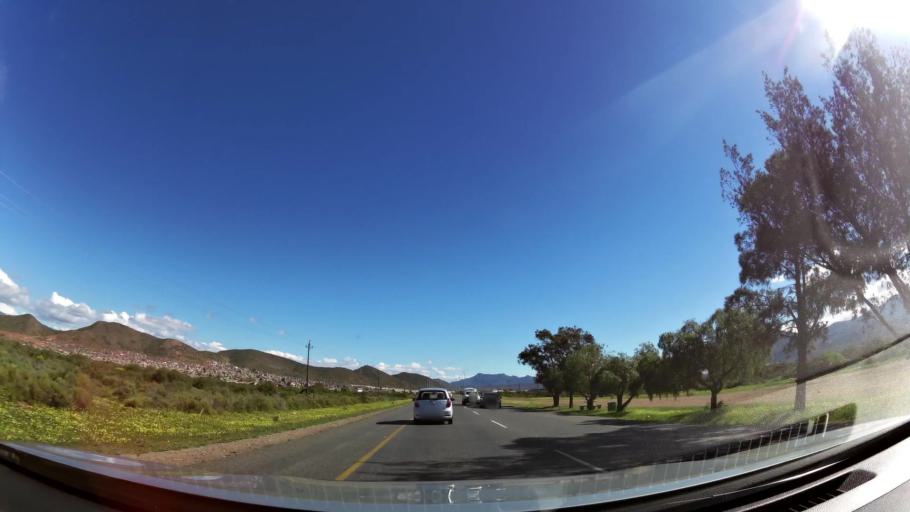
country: ZA
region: Western Cape
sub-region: Cape Winelands District Municipality
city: Ashton
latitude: -33.8148
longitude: 19.9065
